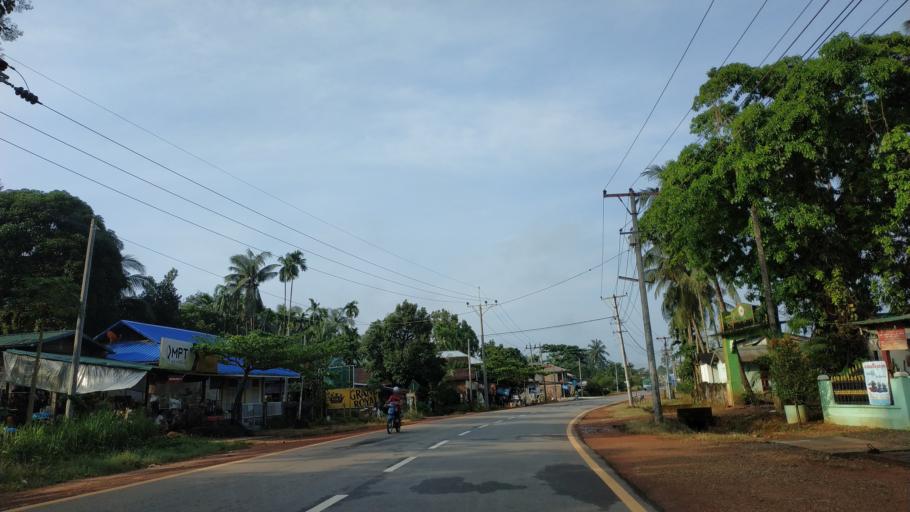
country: MM
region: Tanintharyi
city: Dawei
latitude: 14.2492
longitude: 98.2045
